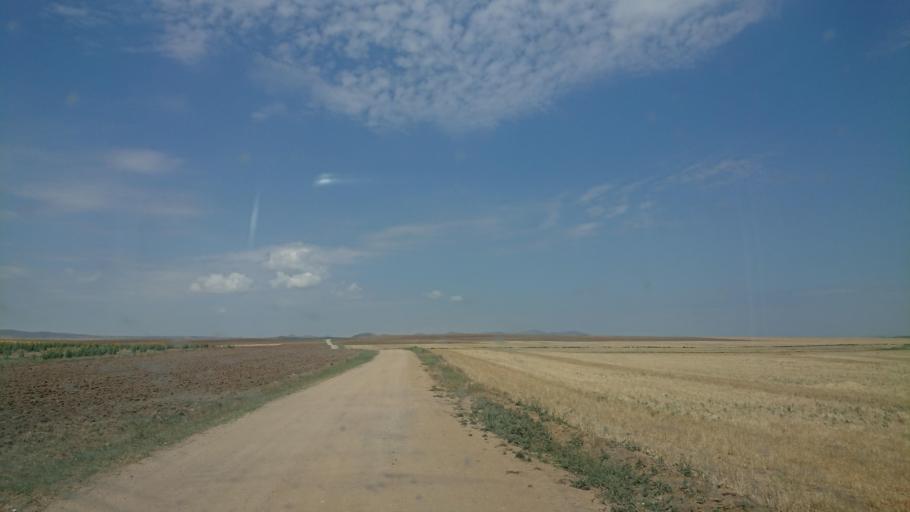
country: TR
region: Aksaray
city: Agacoren
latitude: 38.9547
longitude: 33.9366
